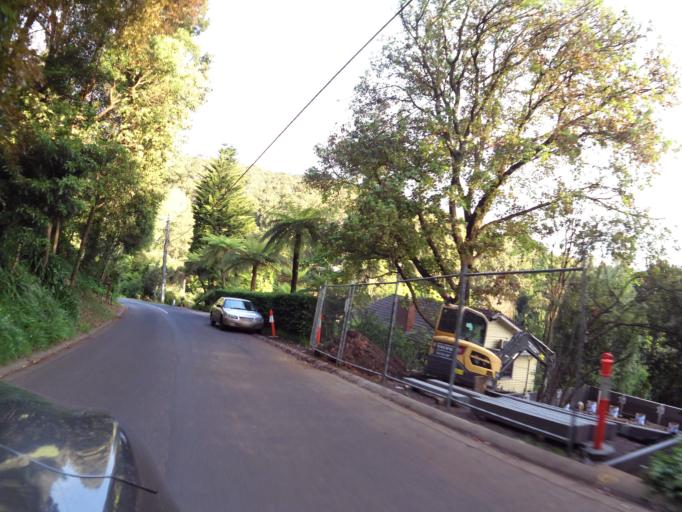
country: AU
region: Victoria
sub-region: Yarra Ranges
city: Tecoma
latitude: -37.8982
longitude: 145.3450
